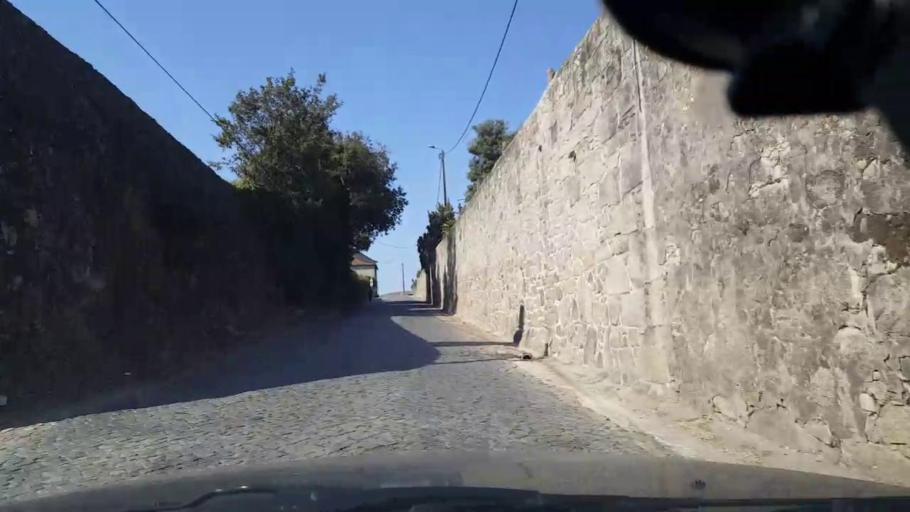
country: PT
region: Porto
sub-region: Vila do Conde
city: Arvore
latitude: 41.3896
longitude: -8.6885
